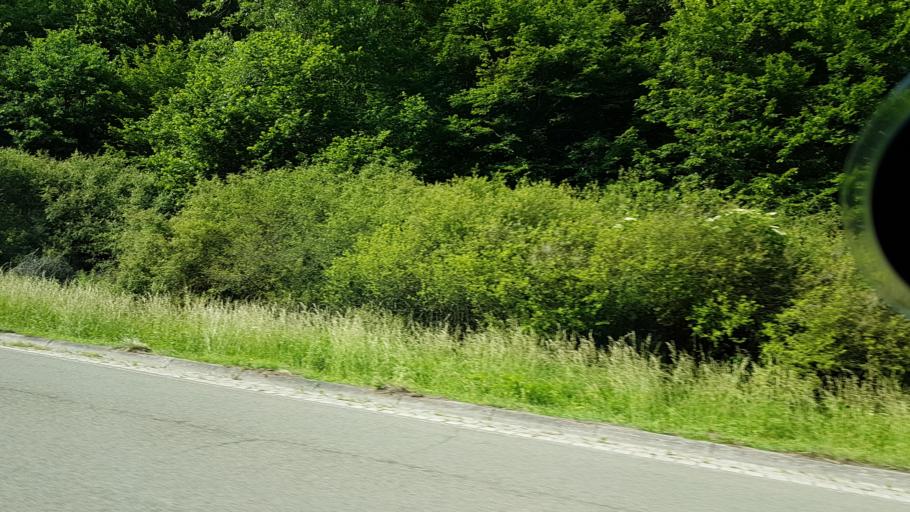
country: DE
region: Rheinland-Pfalz
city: Oberalben
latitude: 49.6024
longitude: 7.4081
